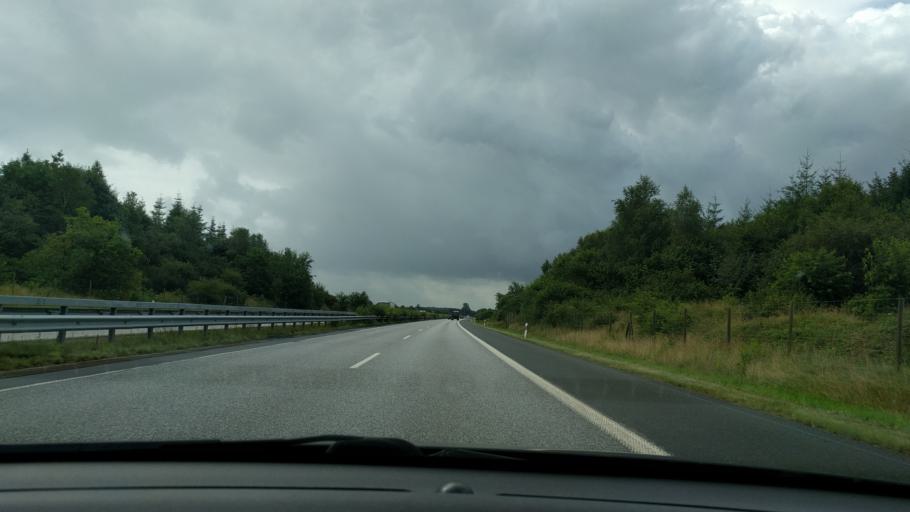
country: DE
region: Schleswig-Holstein
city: Tensbuttel-Rost
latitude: 54.0971
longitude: 9.2660
